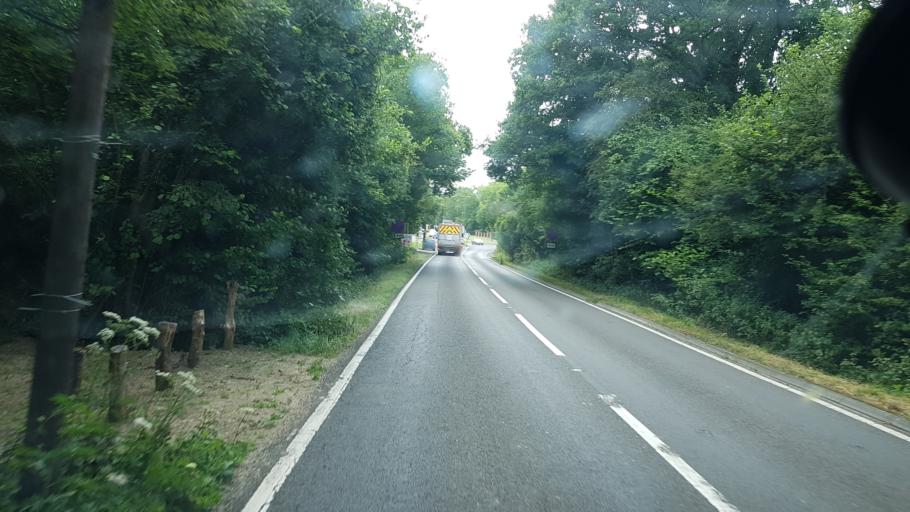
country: GB
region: England
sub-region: Surrey
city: Felbridge
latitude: 51.1659
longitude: -0.0501
